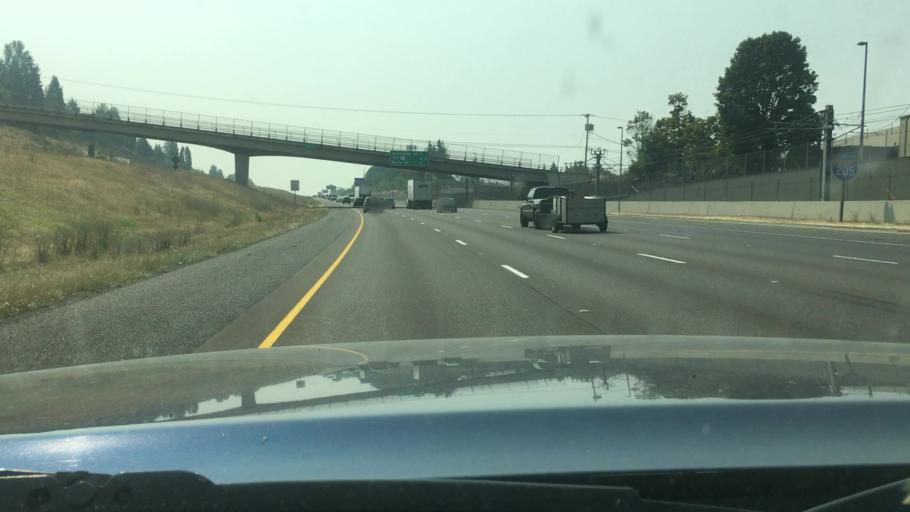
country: US
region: Oregon
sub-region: Multnomah County
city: Lents
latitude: 45.4527
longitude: -122.5730
